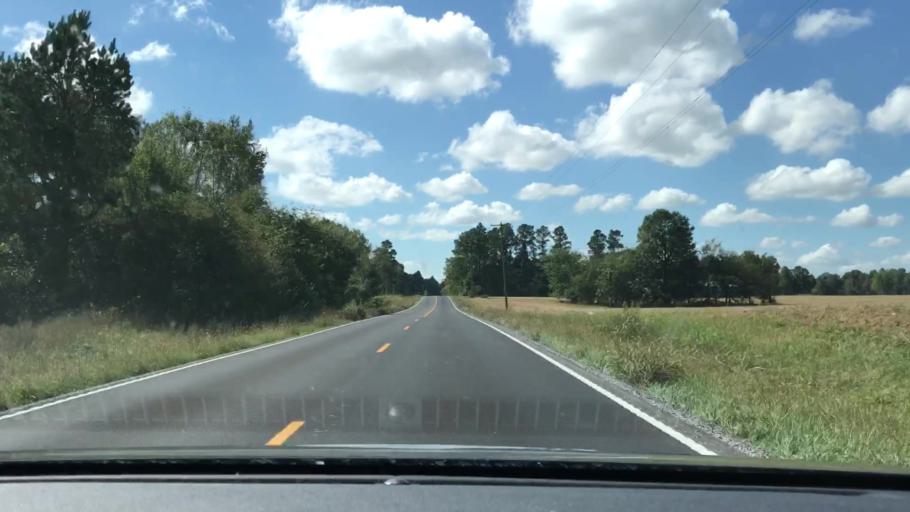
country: US
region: Kentucky
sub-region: McCracken County
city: Reidland
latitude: 36.8795
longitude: -88.5605
